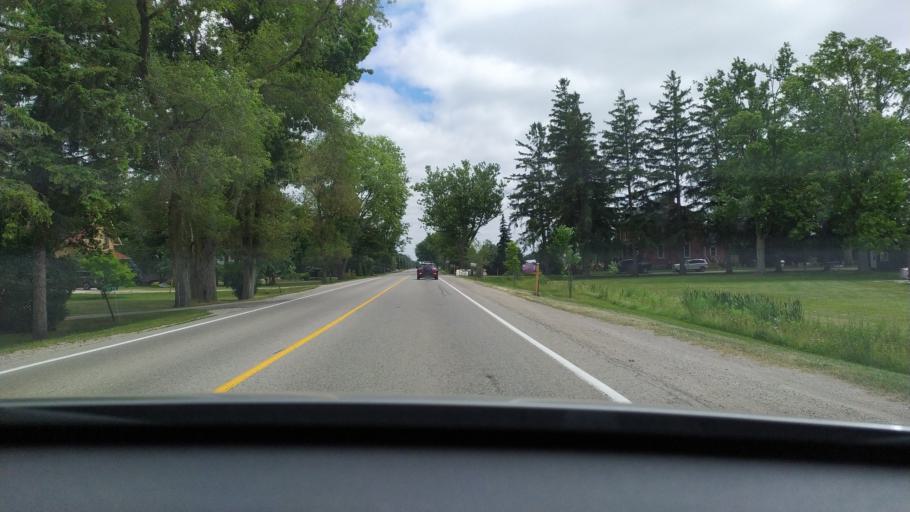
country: CA
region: Ontario
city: Stratford
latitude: 43.3512
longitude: -80.9714
